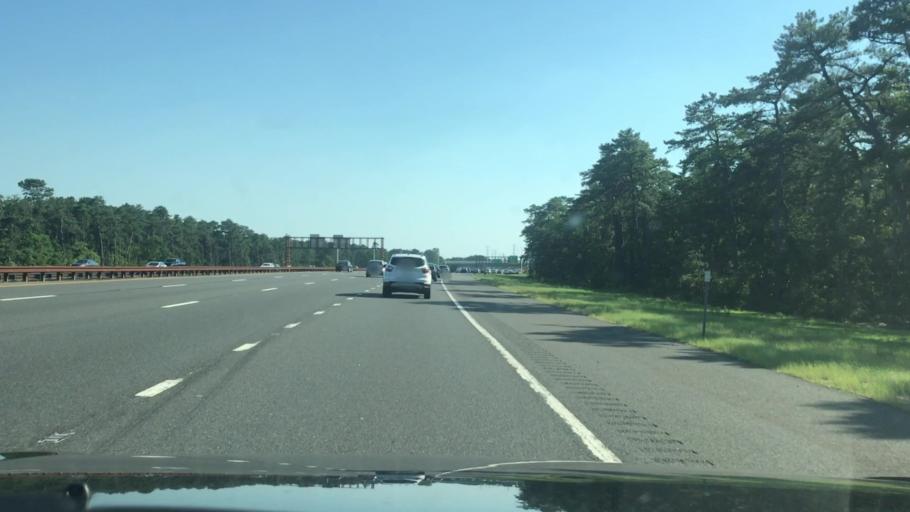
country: US
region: New Jersey
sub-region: Ocean County
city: Leisure Village
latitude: 40.0715
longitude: -74.1582
